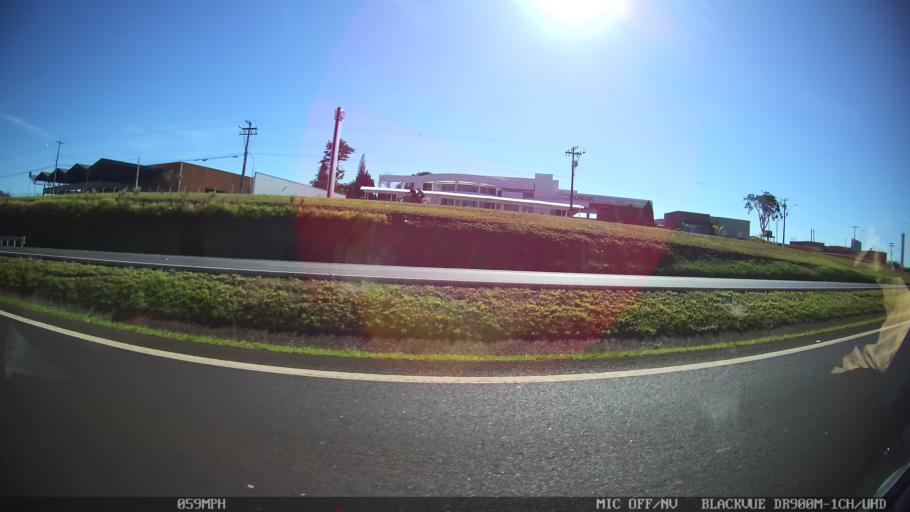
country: BR
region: Sao Paulo
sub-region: Franca
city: Franca
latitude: -20.5691
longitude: -47.4016
